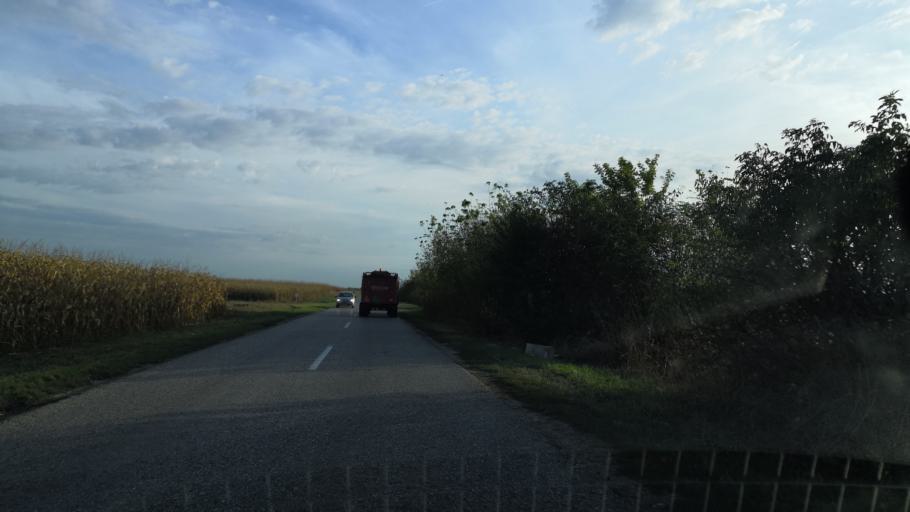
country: RS
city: Novi Karlovci
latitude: 45.0599
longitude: 20.1793
